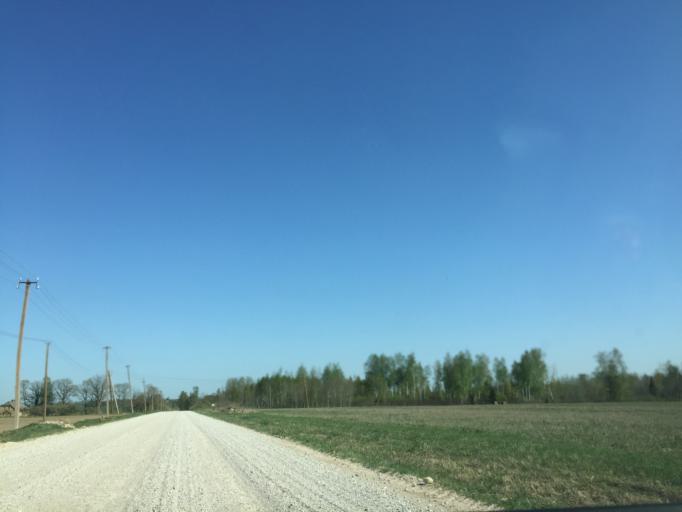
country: LV
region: Malpils
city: Malpils
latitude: 56.8521
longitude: 25.0552
